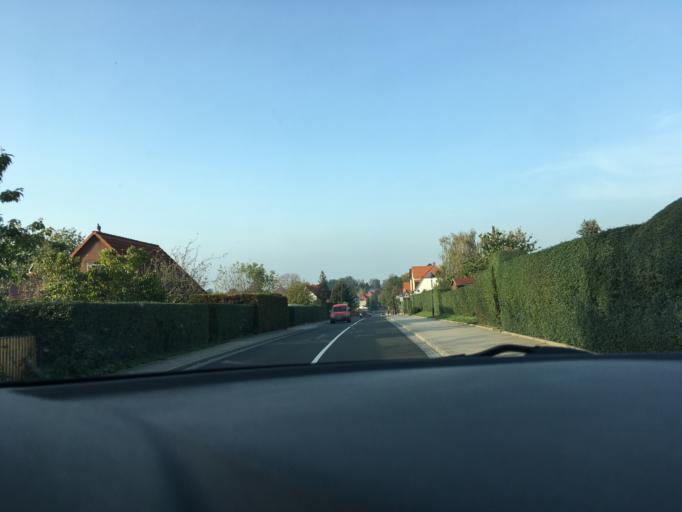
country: DE
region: Saxony
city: Rotha
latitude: 51.1922
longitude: 12.4197
